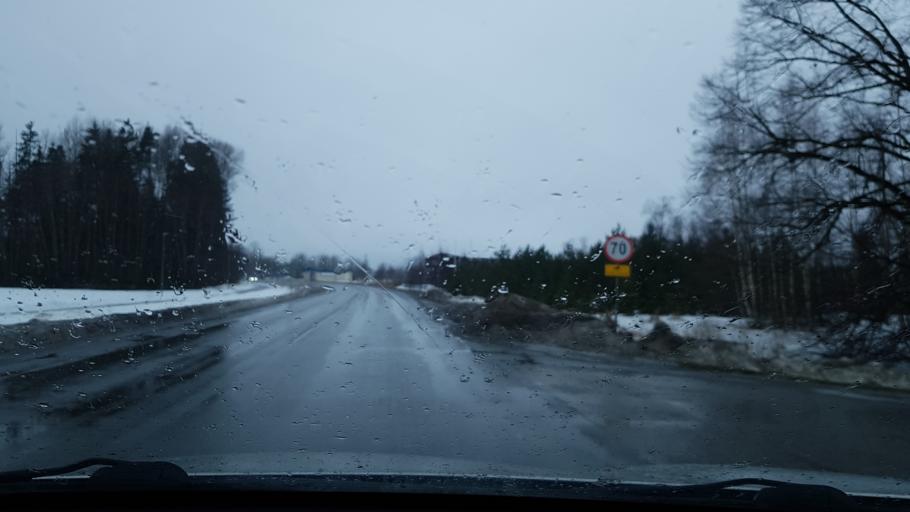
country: EE
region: Raplamaa
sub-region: Kohila vald
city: Kohila
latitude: 59.1706
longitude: 24.7707
